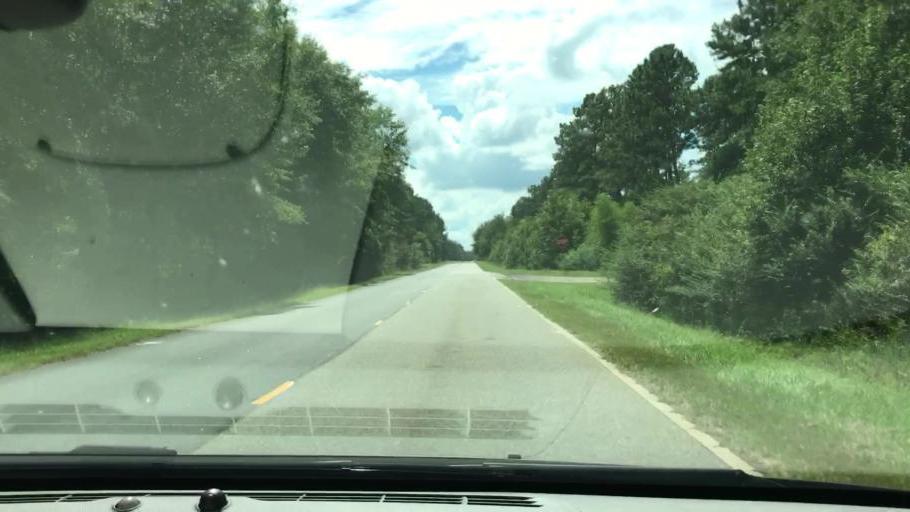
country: US
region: Georgia
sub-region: Quitman County
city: Georgetown
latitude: 32.0012
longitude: -85.0373
